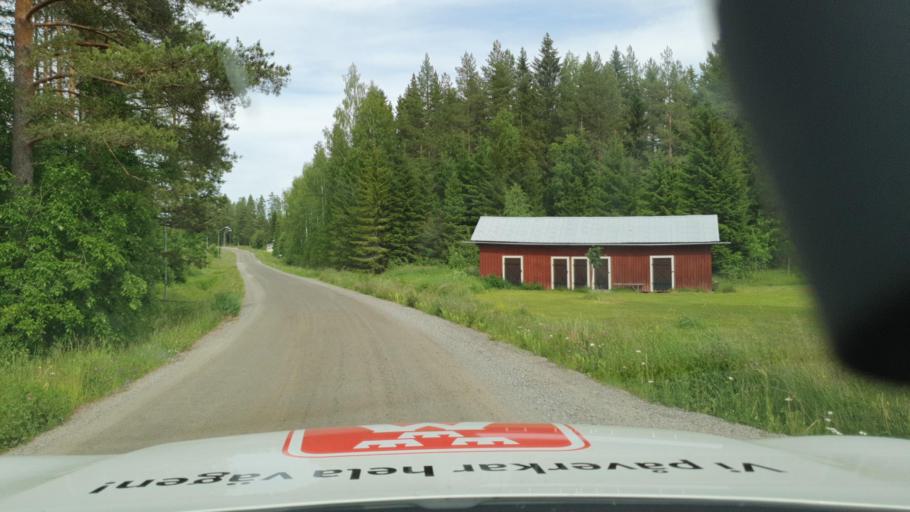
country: SE
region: Vaesterbotten
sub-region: Skelleftea Kommun
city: Viken
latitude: 64.5007
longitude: 20.9233
